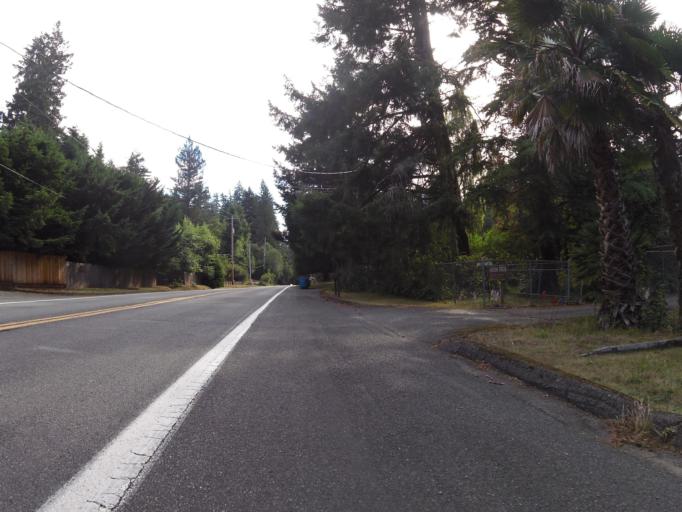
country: US
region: California
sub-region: Del Norte County
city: Bertsch-Oceanview
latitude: 41.8097
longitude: -124.0791
